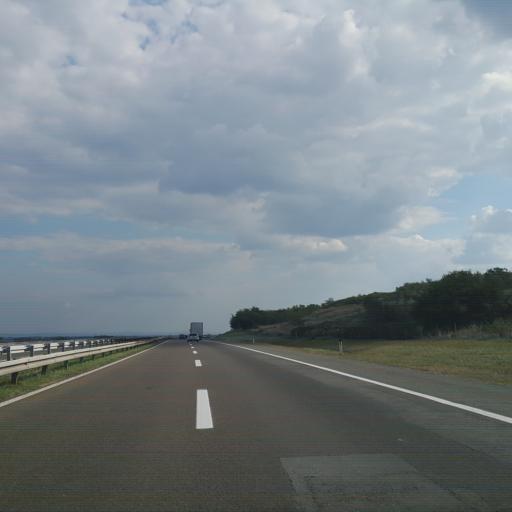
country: RS
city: Lugavcina
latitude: 44.5292
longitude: 21.0047
